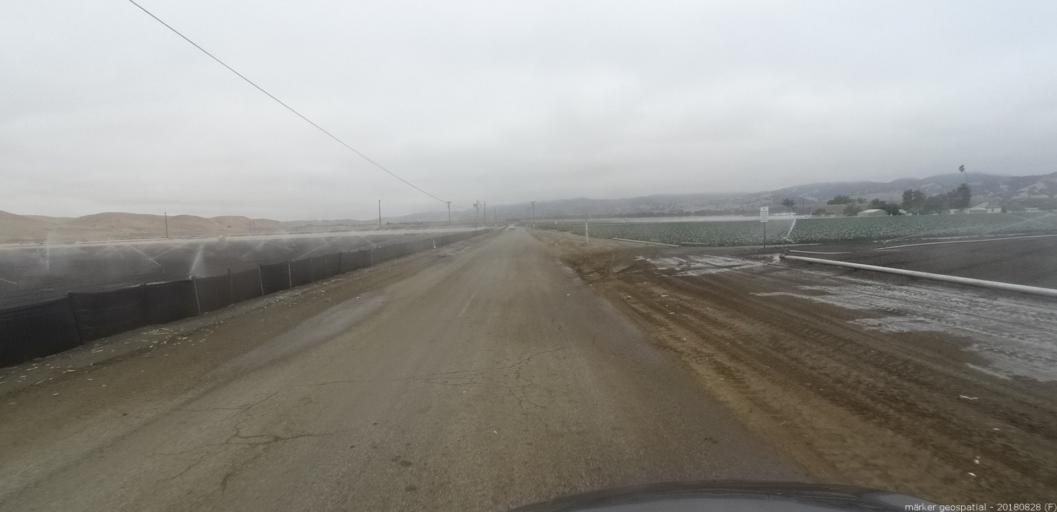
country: US
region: California
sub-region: San Luis Obispo County
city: Lake Nacimiento
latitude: 36.0130
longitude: -120.8862
